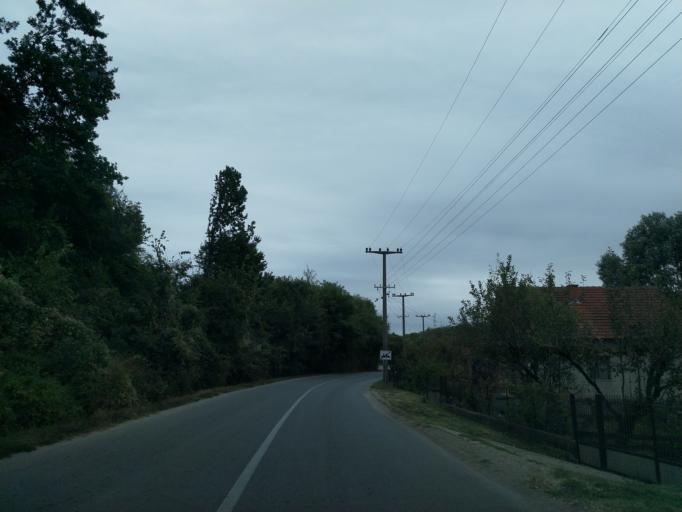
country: RS
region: Central Serbia
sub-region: Pomoravski Okrug
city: Jagodina
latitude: 44.0526
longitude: 21.1808
